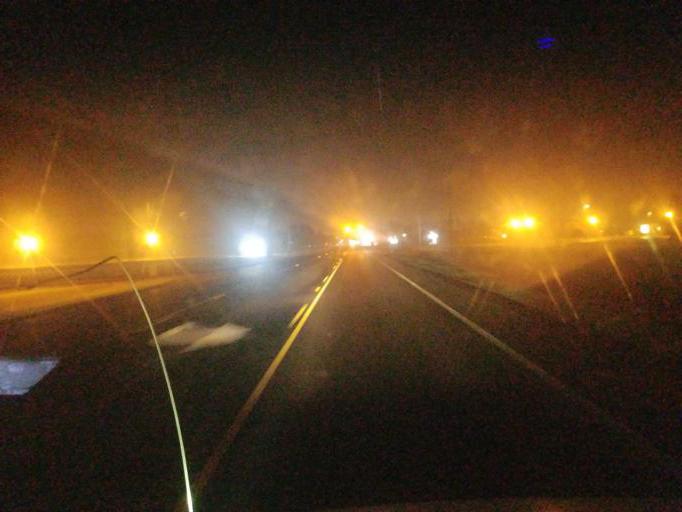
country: US
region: Ohio
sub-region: Erie County
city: Sandusky
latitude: 41.4255
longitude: -82.7185
